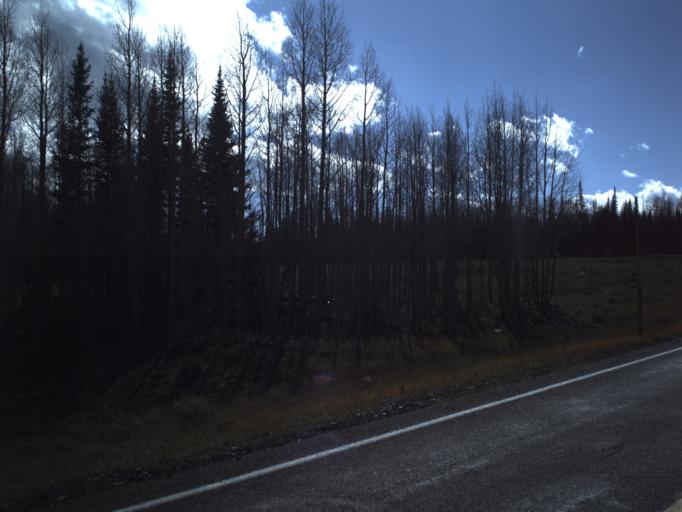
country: US
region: Utah
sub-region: Iron County
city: Parowan
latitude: 37.6550
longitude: -112.7612
